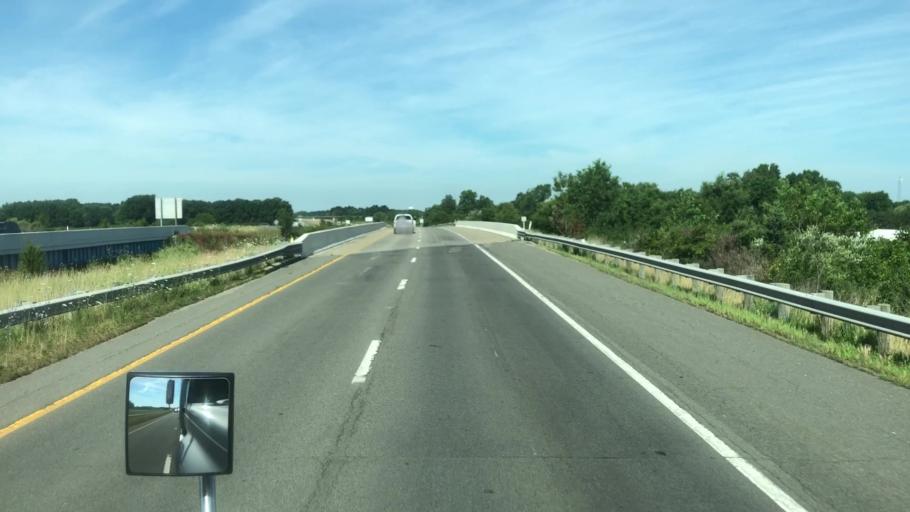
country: US
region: Ohio
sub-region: Erie County
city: Huron
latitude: 41.4061
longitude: -82.6026
